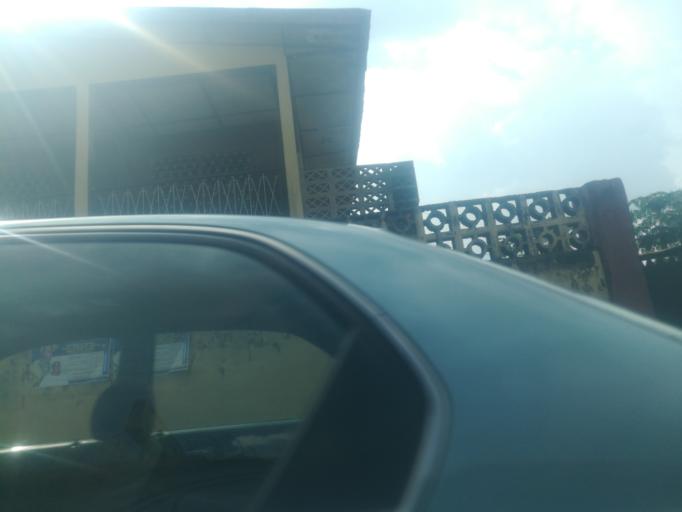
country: NG
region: Oyo
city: Ibadan
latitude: 7.3489
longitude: 3.8764
